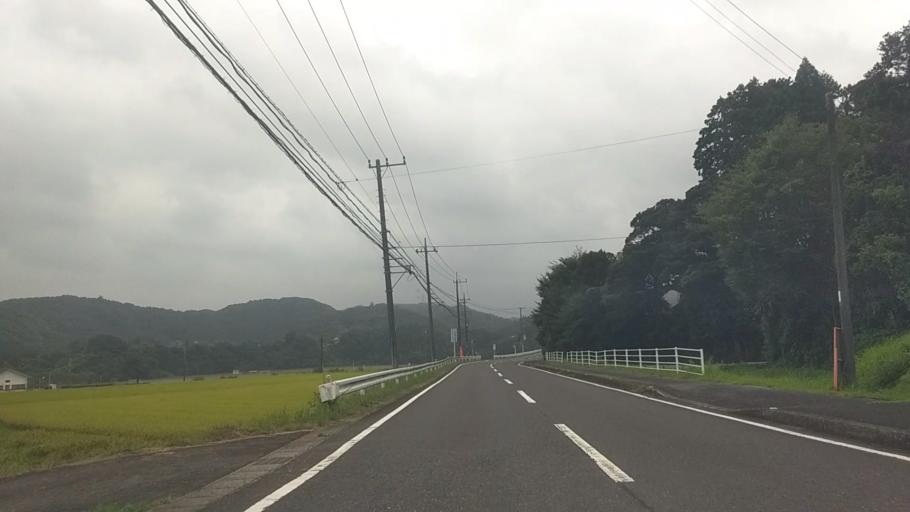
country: JP
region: Chiba
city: Kawaguchi
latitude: 35.2593
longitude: 140.0536
